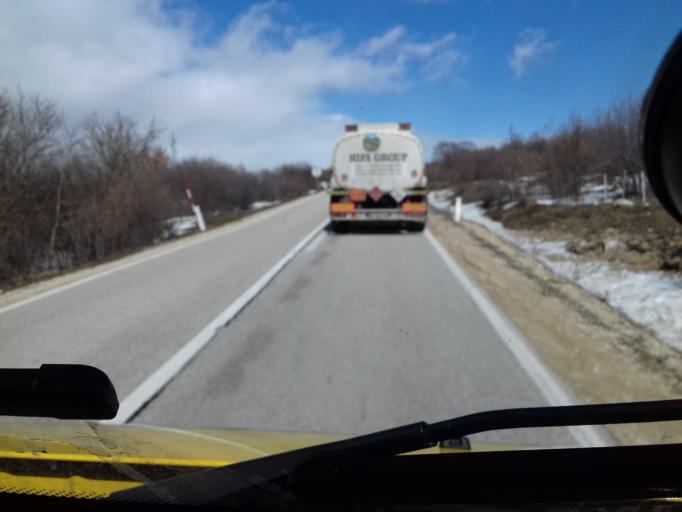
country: BA
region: Federation of Bosnia and Herzegovina
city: Tomislavgrad
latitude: 43.7835
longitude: 17.2222
